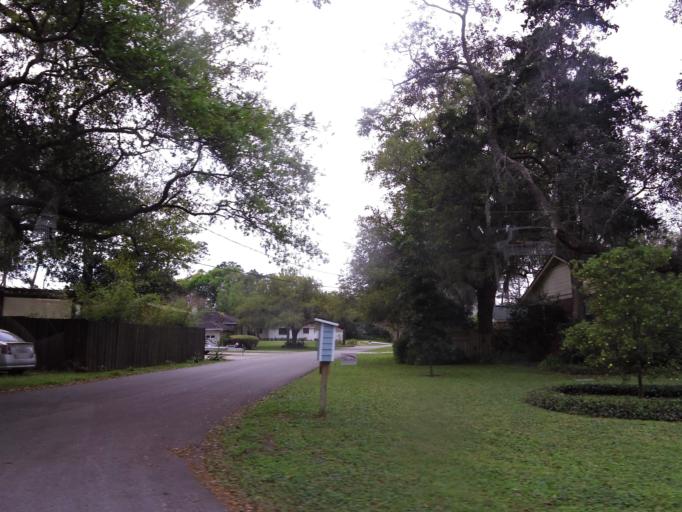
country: US
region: Florida
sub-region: Duval County
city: Jacksonville
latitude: 30.2749
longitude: -81.6459
